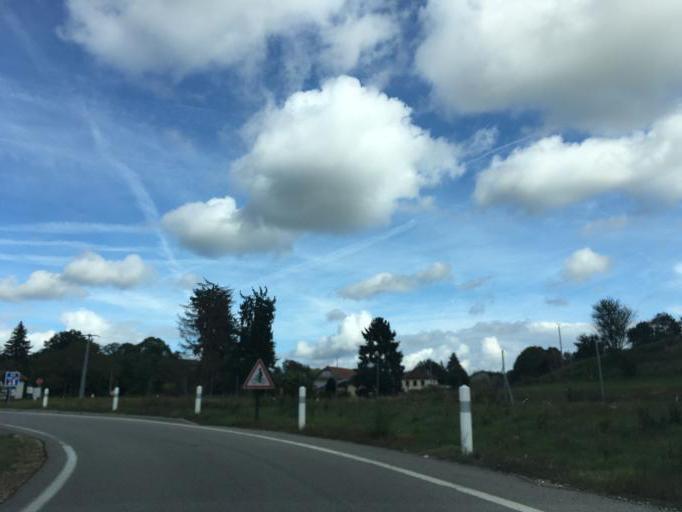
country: FR
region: Rhone-Alpes
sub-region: Departement de l'Isere
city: Saint-Didier-de-la-Tour
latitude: 45.5566
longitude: 5.4661
